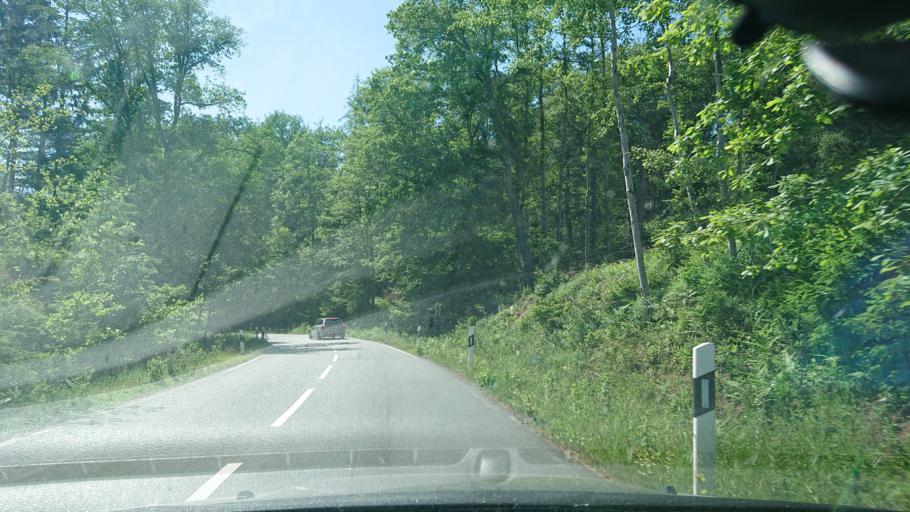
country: DE
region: North Rhine-Westphalia
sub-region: Regierungsbezirk Arnsberg
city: Mohnesee
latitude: 51.4654
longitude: 8.1481
